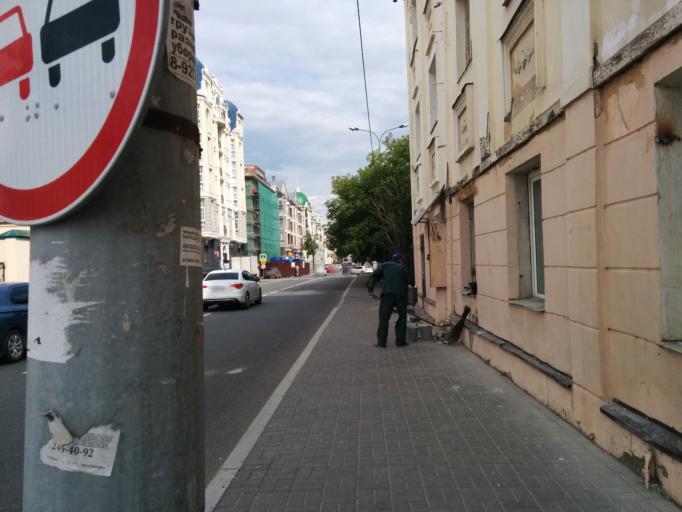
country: RU
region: Tatarstan
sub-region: Gorod Kazan'
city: Kazan
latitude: 55.7962
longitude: 49.1125
